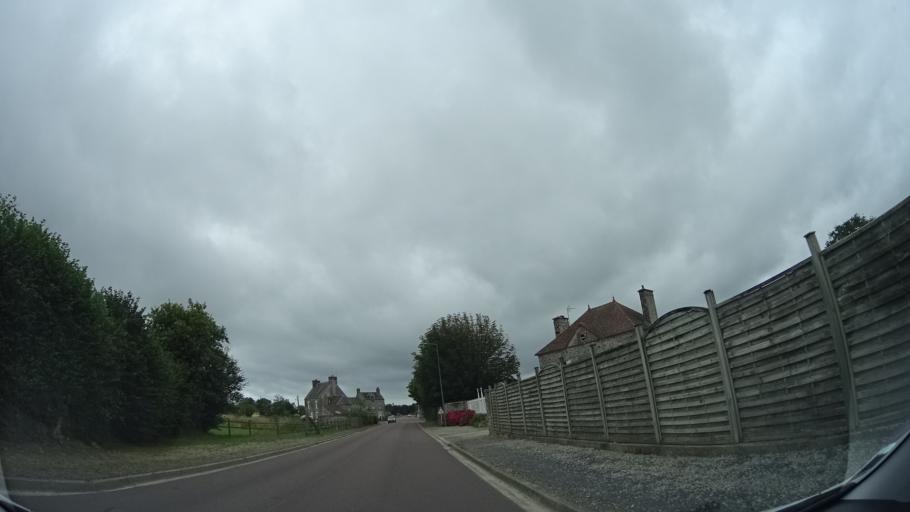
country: FR
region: Lower Normandy
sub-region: Departement de la Manche
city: La Haye-du-Puits
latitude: 49.3006
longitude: -1.5742
